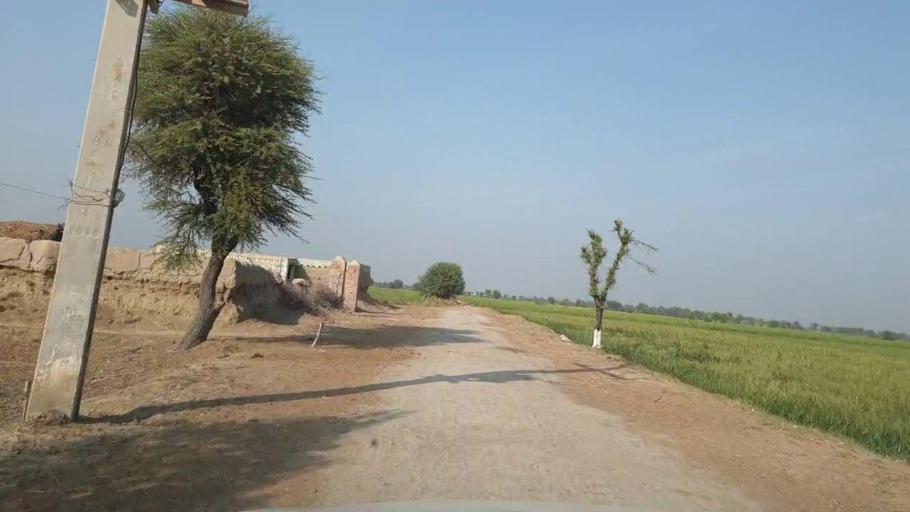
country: PK
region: Sindh
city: Pithoro
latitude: 25.6895
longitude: 69.2076
